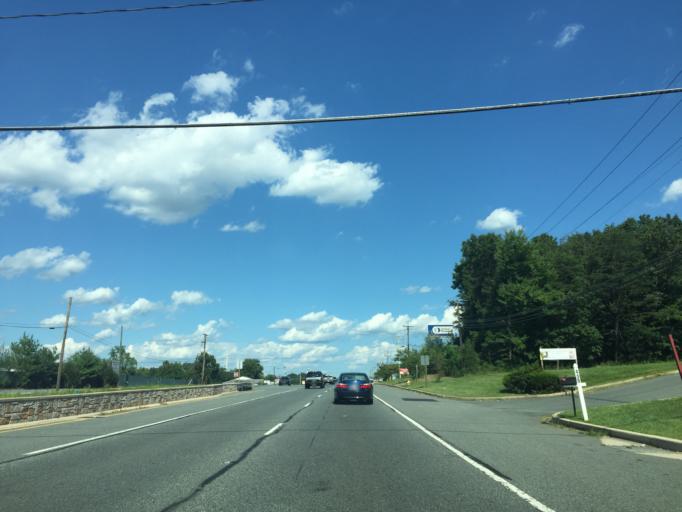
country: US
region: Maryland
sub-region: Harford County
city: Joppatowne
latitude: 39.4280
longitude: -76.3618
